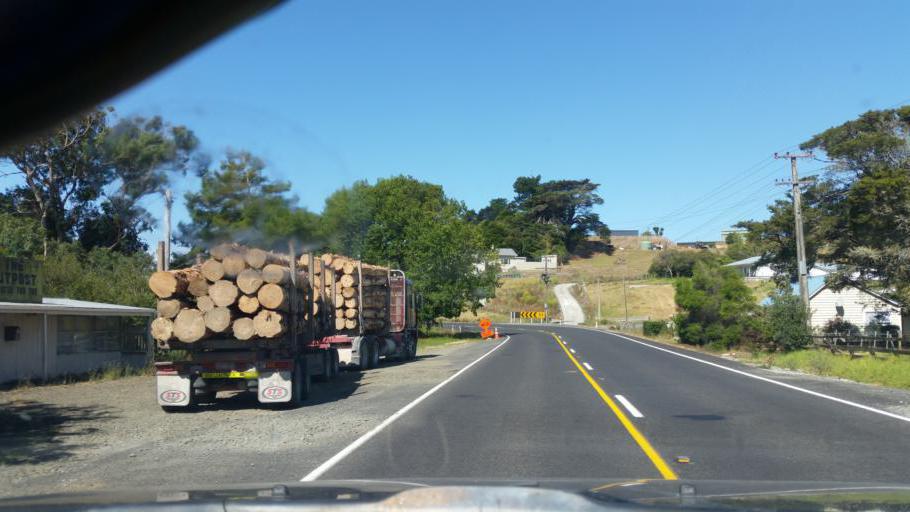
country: NZ
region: Northland
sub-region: Kaipara District
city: Dargaville
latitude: -35.9529
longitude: 173.8533
